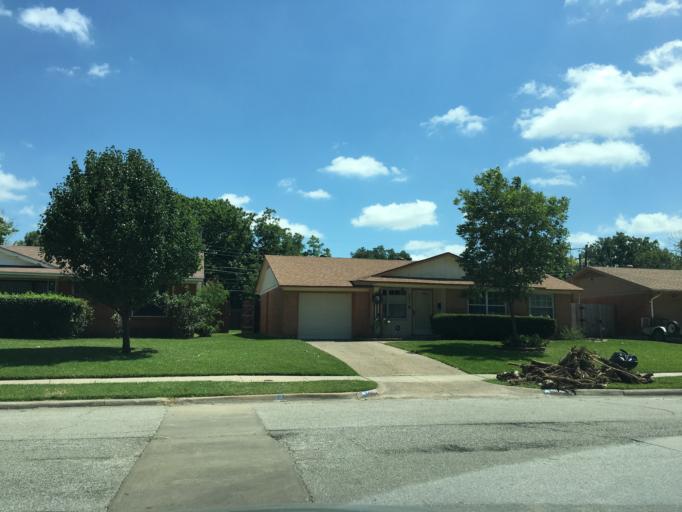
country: US
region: Texas
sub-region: Dallas County
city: Garland
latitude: 32.8363
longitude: -96.6545
